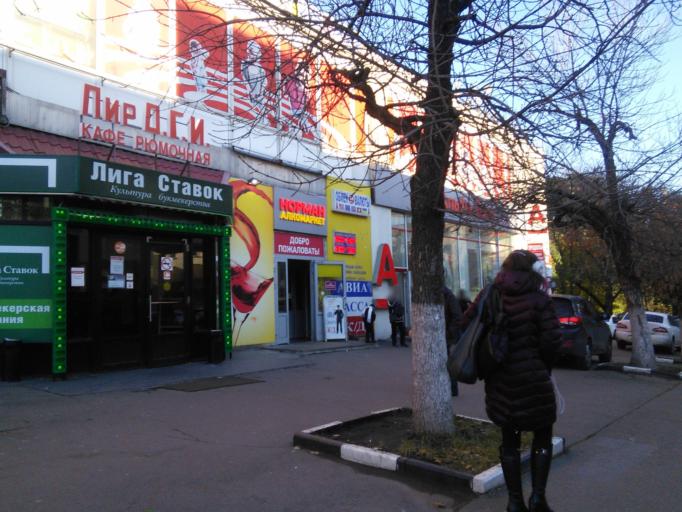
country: RU
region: Moskovskaya
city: Cheremushki
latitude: 55.6705
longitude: 37.5557
